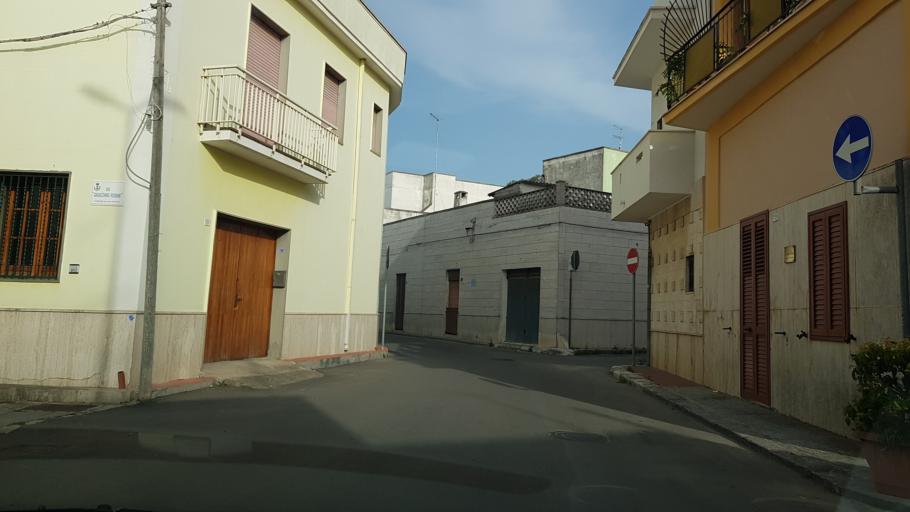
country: IT
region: Apulia
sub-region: Provincia di Brindisi
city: San Donaci
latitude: 40.4460
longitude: 17.9220
